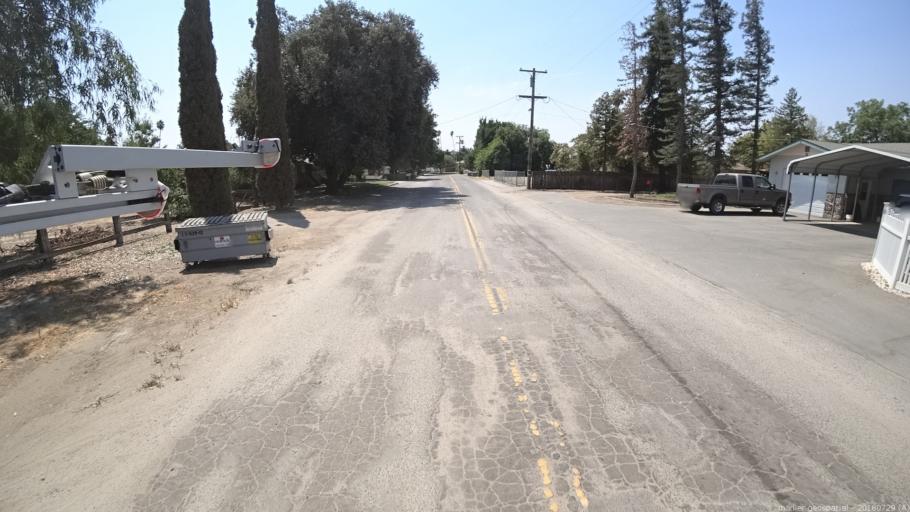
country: US
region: California
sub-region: Madera County
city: Chowchilla
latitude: 37.0899
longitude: -120.2938
